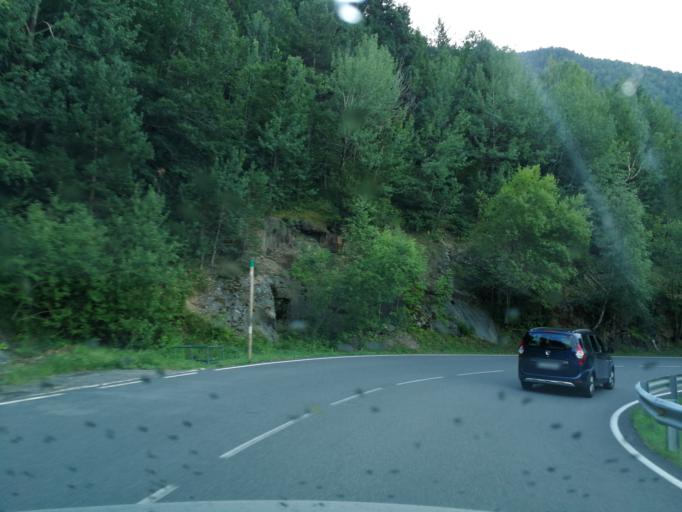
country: AD
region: Ordino
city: Ordino
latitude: 42.5544
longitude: 1.5412
